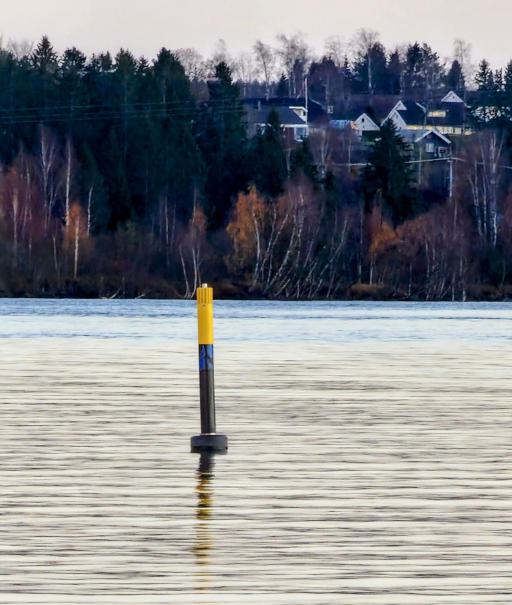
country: NO
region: Akershus
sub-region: Nes
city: Arnes
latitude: 60.1468
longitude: 11.4596
